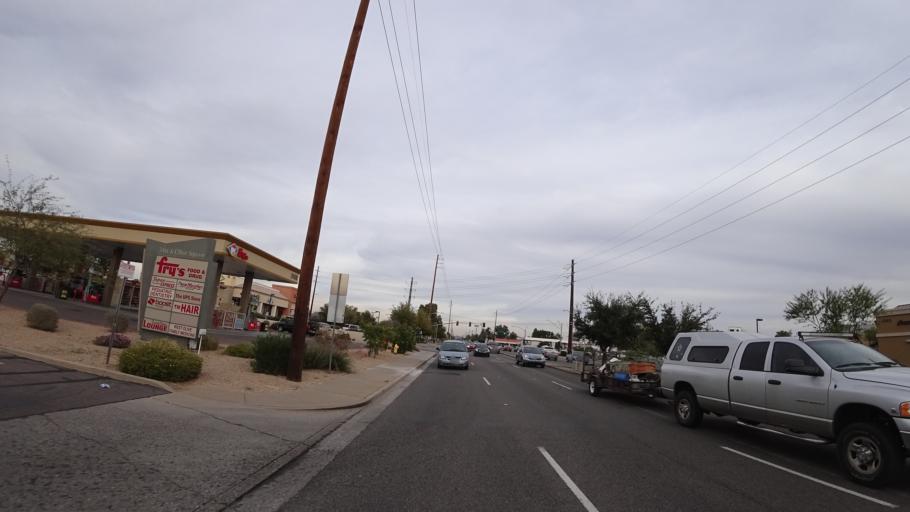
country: US
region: Arizona
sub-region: Maricopa County
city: Glendale
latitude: 33.5676
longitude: -112.1702
